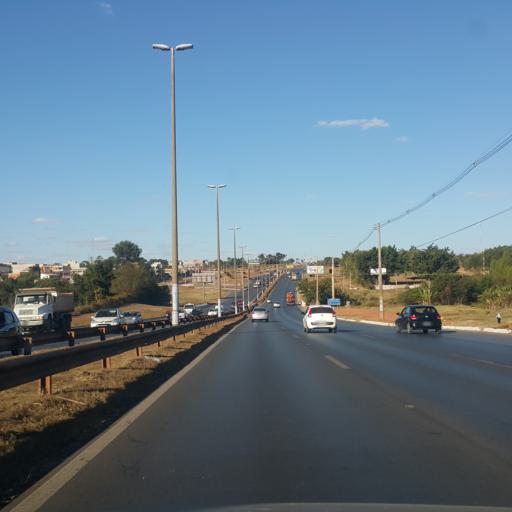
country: BR
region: Federal District
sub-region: Brasilia
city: Brasilia
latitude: -15.7865
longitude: -48.0051
